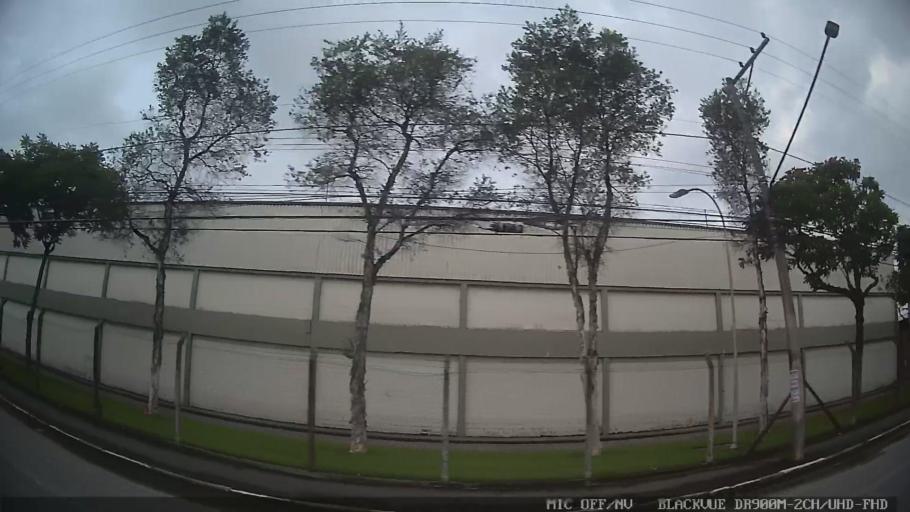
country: BR
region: Sao Paulo
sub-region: Suzano
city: Suzano
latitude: -23.5349
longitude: -46.2900
